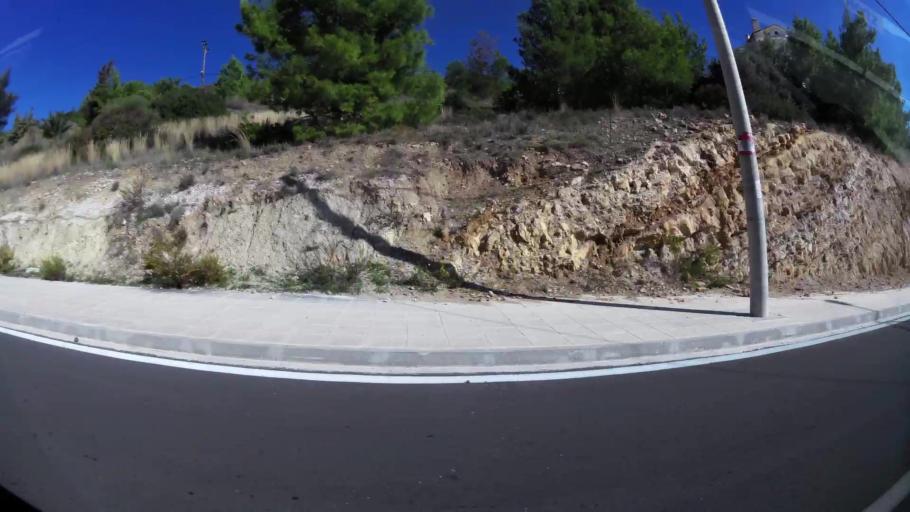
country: GR
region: Attica
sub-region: Nomarchia Anatolikis Attikis
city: Dhrafi
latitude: 38.0129
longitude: 23.9113
